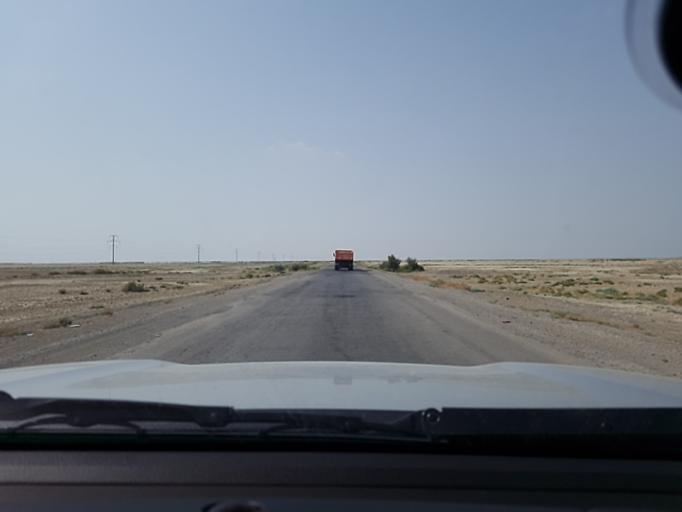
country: TM
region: Balkan
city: Gumdag
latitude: 38.9174
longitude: 54.5913
